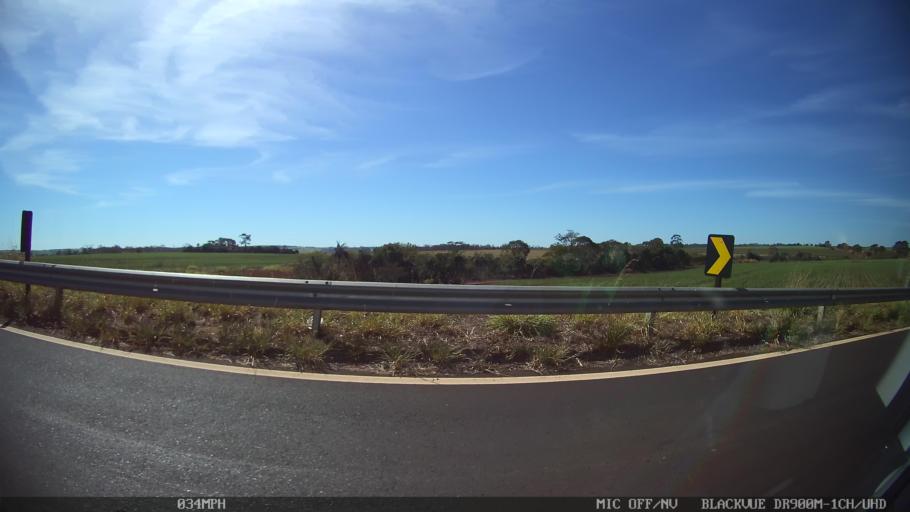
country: BR
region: Sao Paulo
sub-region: Nuporanga
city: Nuporanga
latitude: -20.5608
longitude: -47.6242
